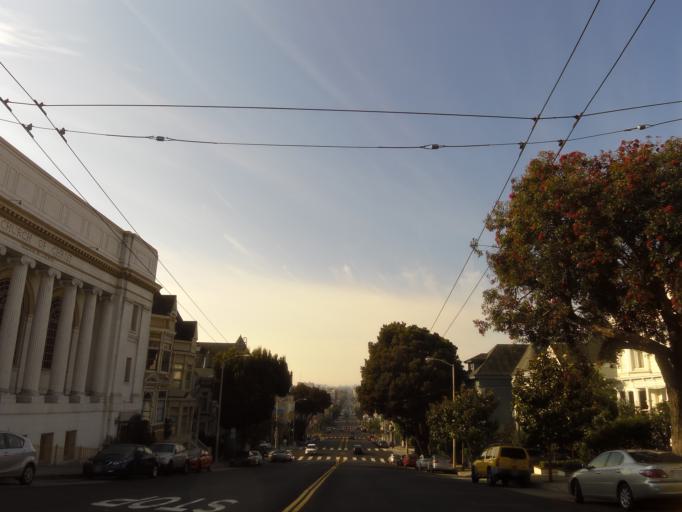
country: US
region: California
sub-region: San Francisco County
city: San Francisco
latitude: 37.7898
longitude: -122.4408
